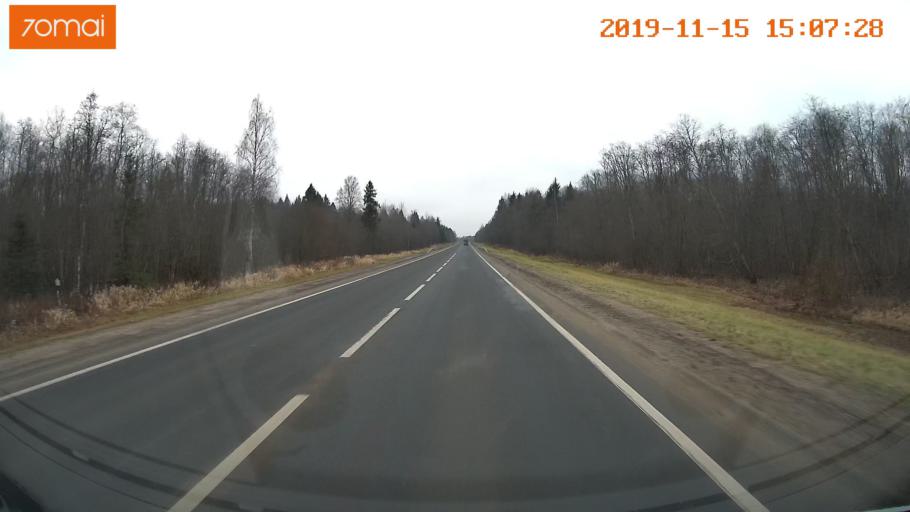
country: RU
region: Jaroslavl
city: Prechistoye
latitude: 58.3832
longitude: 40.2946
